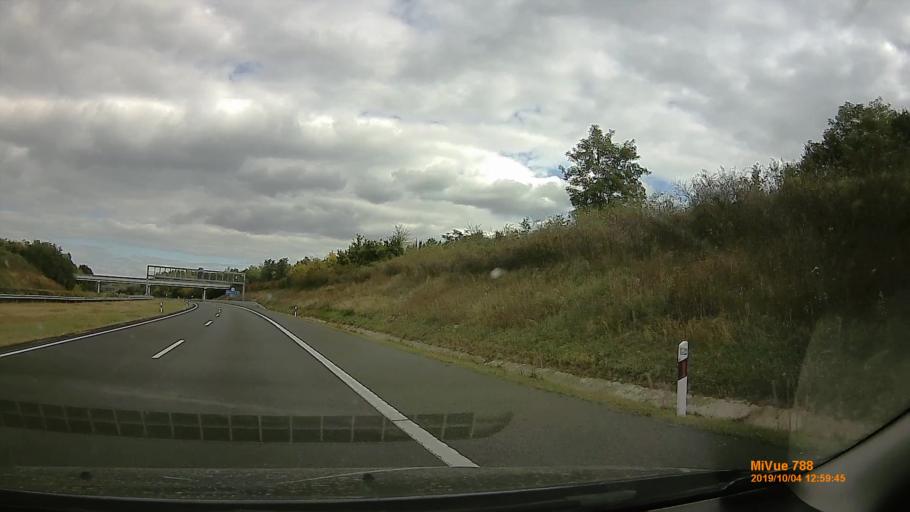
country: HU
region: Somogy
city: Balatonszarszo
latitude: 46.8113
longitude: 17.8439
